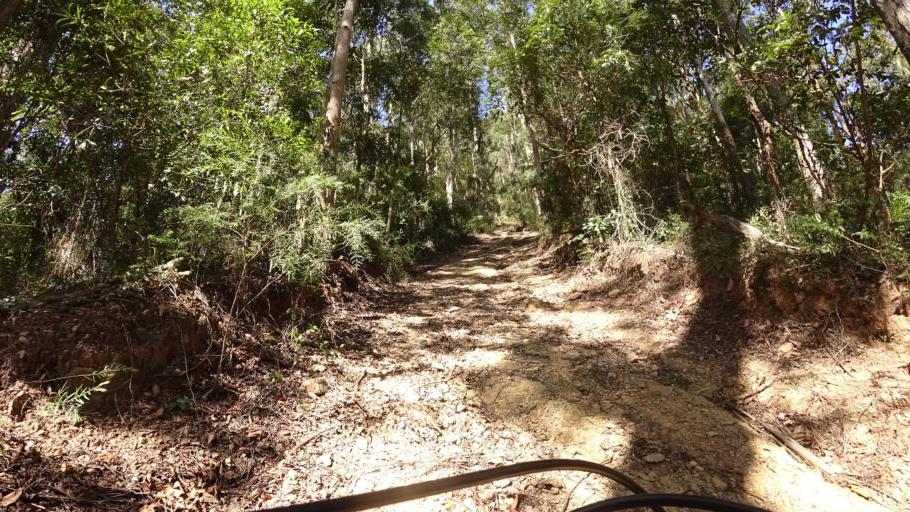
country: AU
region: Queensland
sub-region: Moreton Bay
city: Highvale
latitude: -27.4119
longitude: 152.7860
